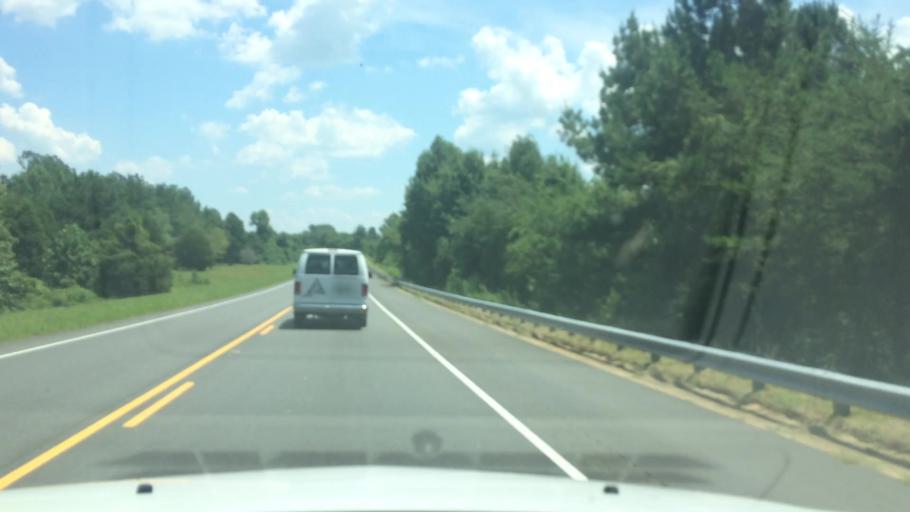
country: US
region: North Carolina
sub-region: Iredell County
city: Statesville
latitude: 35.8065
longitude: -80.9672
